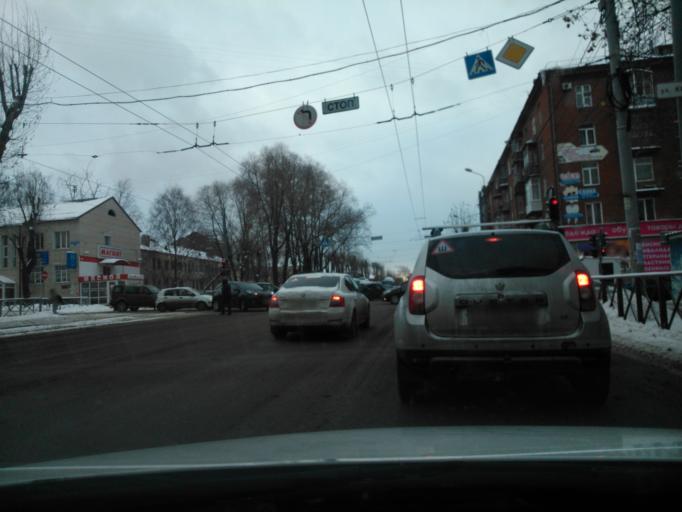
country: RU
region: Perm
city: Perm
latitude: 57.9882
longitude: 56.2486
